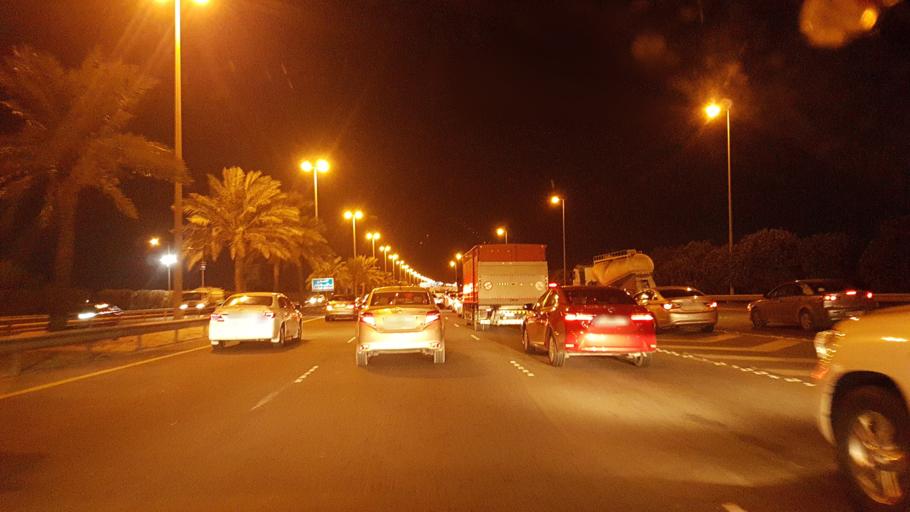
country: BH
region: Northern
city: Madinat `Isa
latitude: 26.1667
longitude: 50.5034
